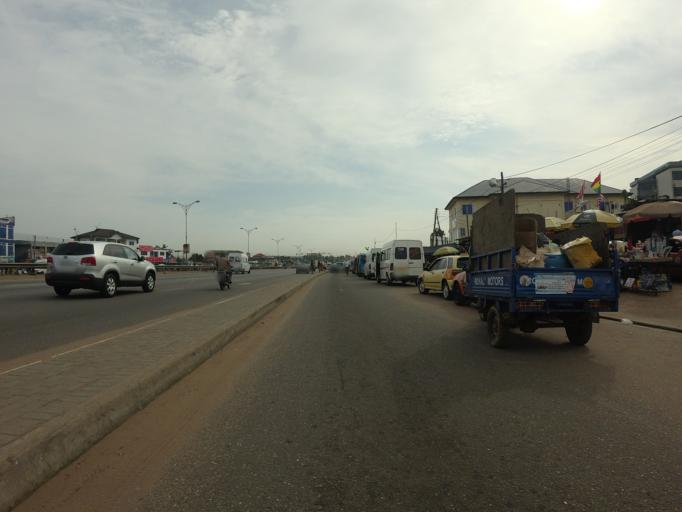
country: GH
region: Greater Accra
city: Dome
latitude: 5.6070
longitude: -0.2479
